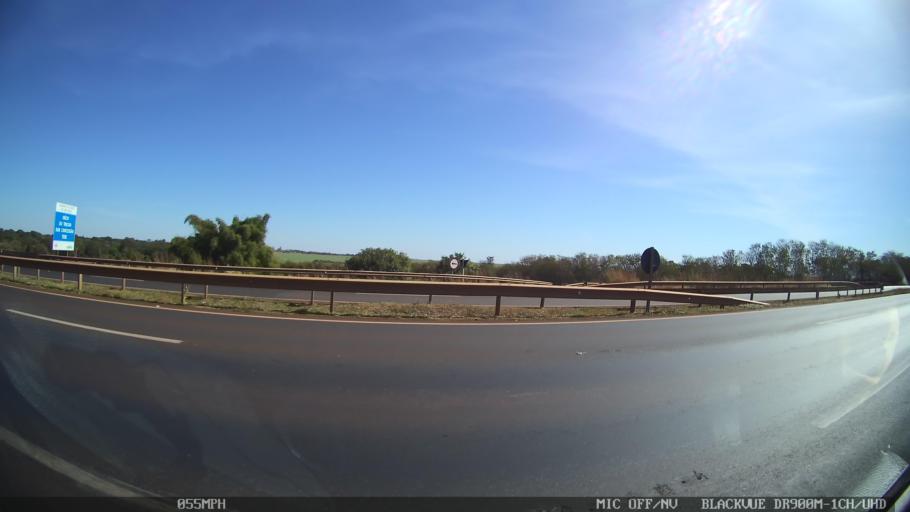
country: BR
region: Sao Paulo
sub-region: Barretos
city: Barretos
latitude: -20.5301
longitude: -48.5973
